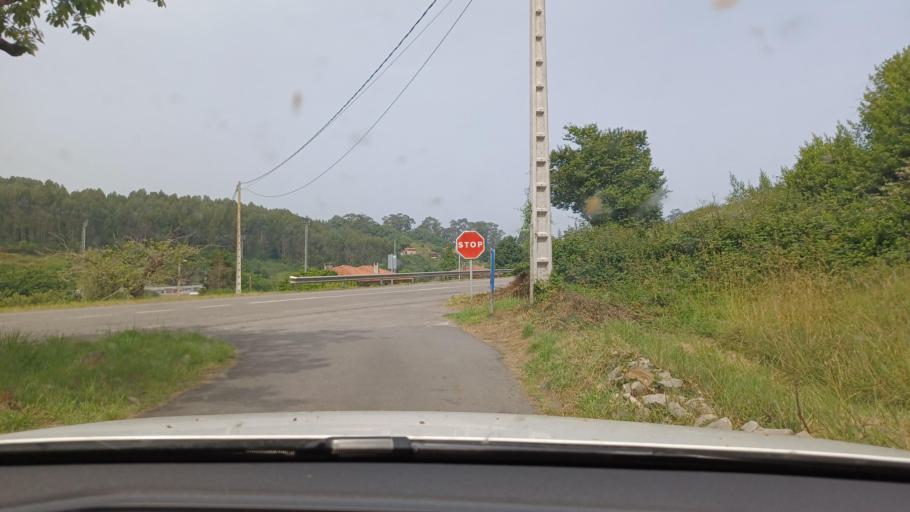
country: ES
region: Asturias
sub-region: Province of Asturias
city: Ribadesella
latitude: 43.4582
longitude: -5.0440
